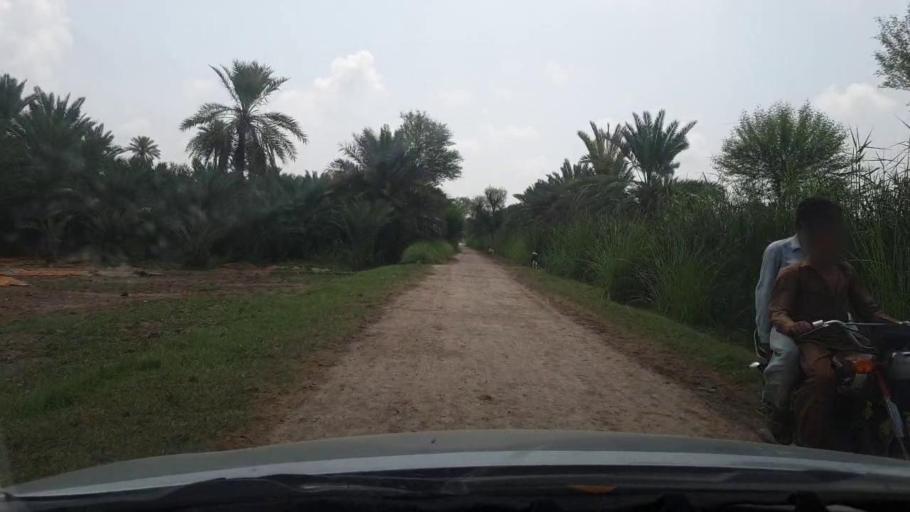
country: PK
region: Sindh
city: Khairpur
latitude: 27.4858
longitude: 68.7286
